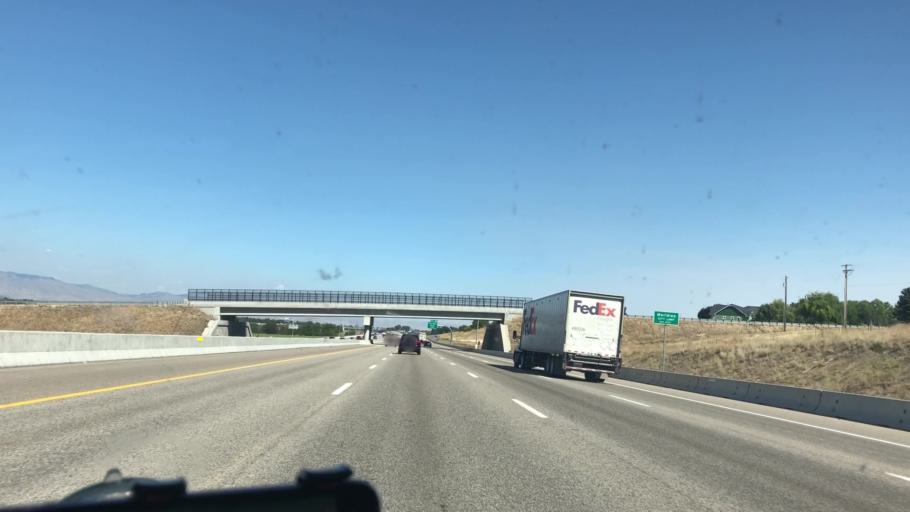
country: US
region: Idaho
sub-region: Ada County
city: Meridian
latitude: 43.5950
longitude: -116.4560
